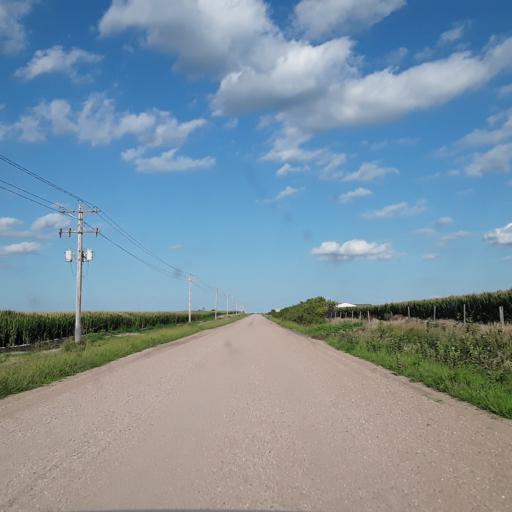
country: US
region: Nebraska
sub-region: Hall County
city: Wood River
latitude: 40.9169
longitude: -98.6057
